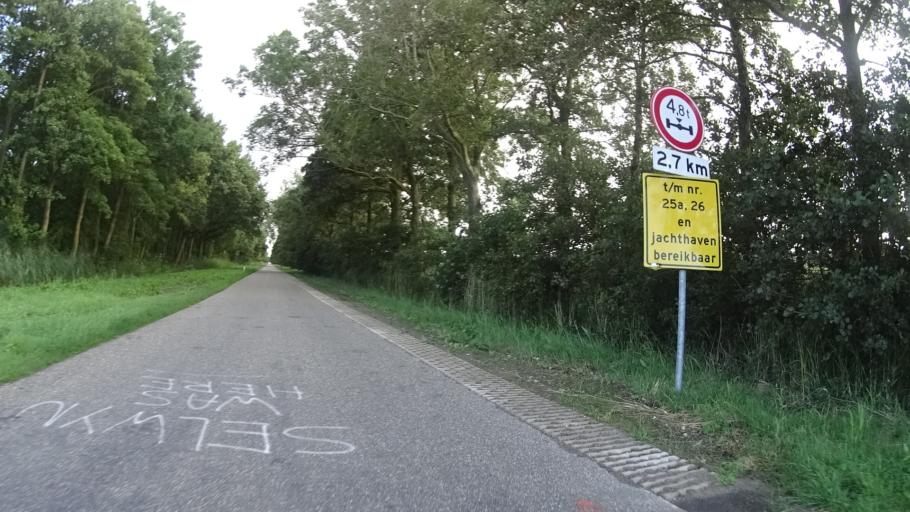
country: NL
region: North Holland
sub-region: Gemeente Hollands Kroon
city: Den Oever
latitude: 52.9074
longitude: 5.0610
